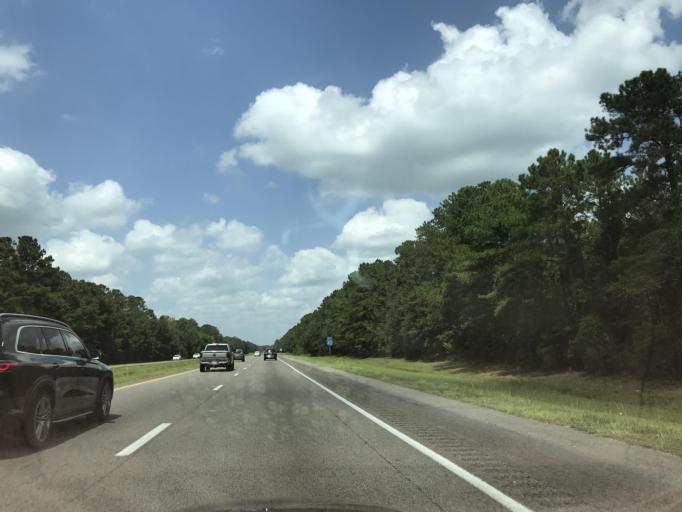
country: US
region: North Carolina
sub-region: Pender County
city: Burgaw
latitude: 34.5908
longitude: -77.9074
